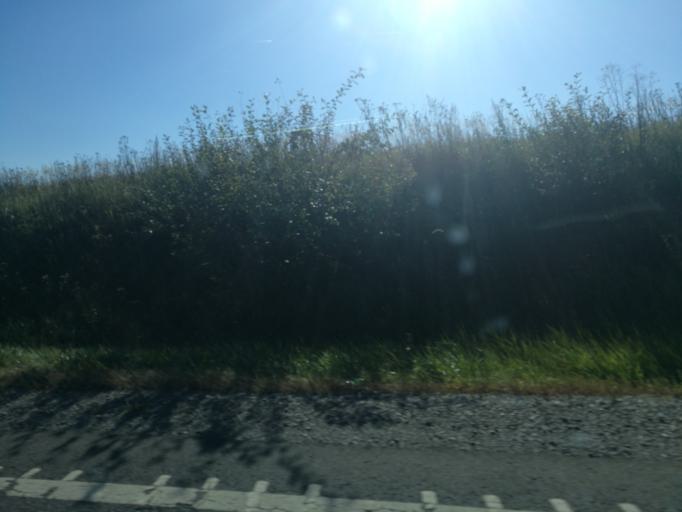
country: RO
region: Brasov
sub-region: Comuna Sercaia
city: Sercaia
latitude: 45.8149
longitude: 25.1653
